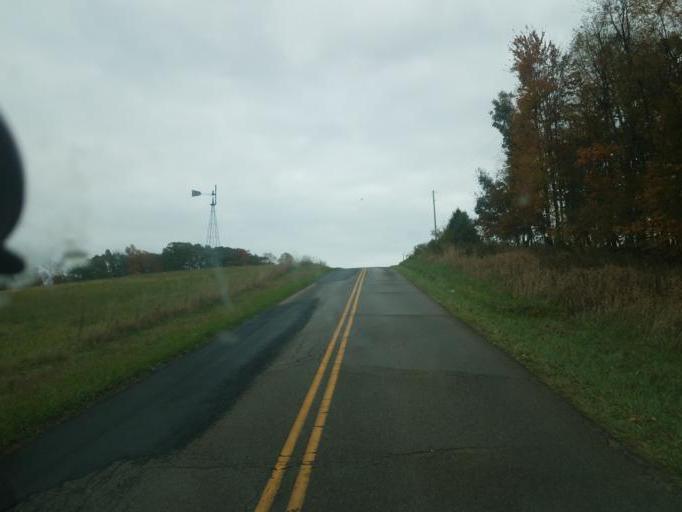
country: US
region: Ohio
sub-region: Knox County
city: Gambier
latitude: 40.4936
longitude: -82.4071
